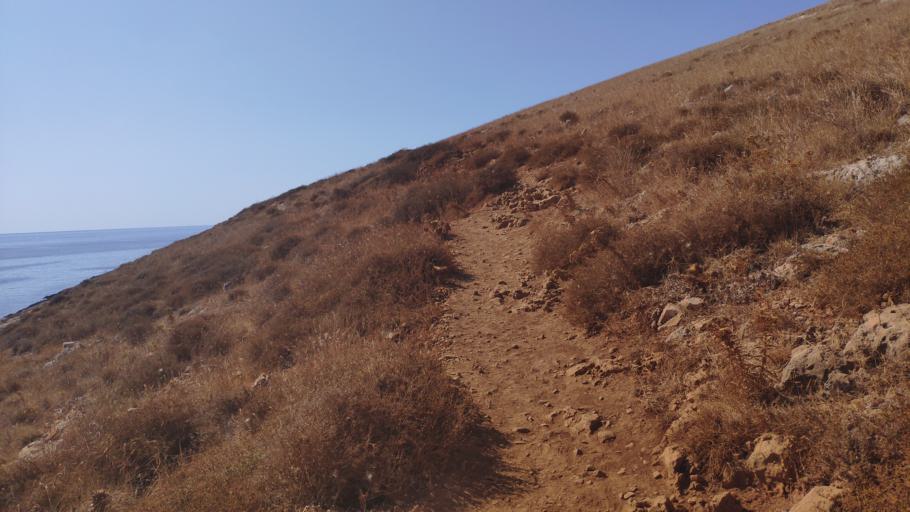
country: GR
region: Peloponnese
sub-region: Nomos Lakonias
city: Gytheio
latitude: 36.3988
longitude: 22.4846
